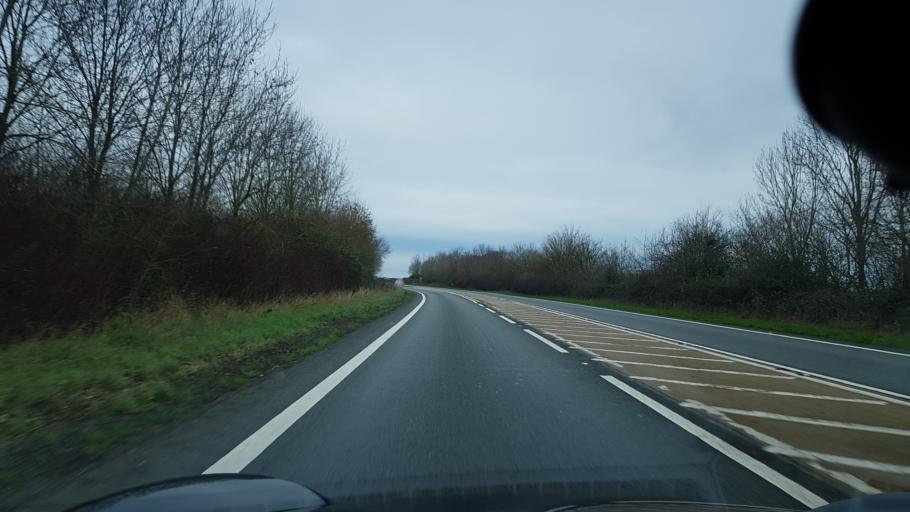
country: GB
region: England
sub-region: Somerset
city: Ilminster
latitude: 50.9518
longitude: -2.9572
